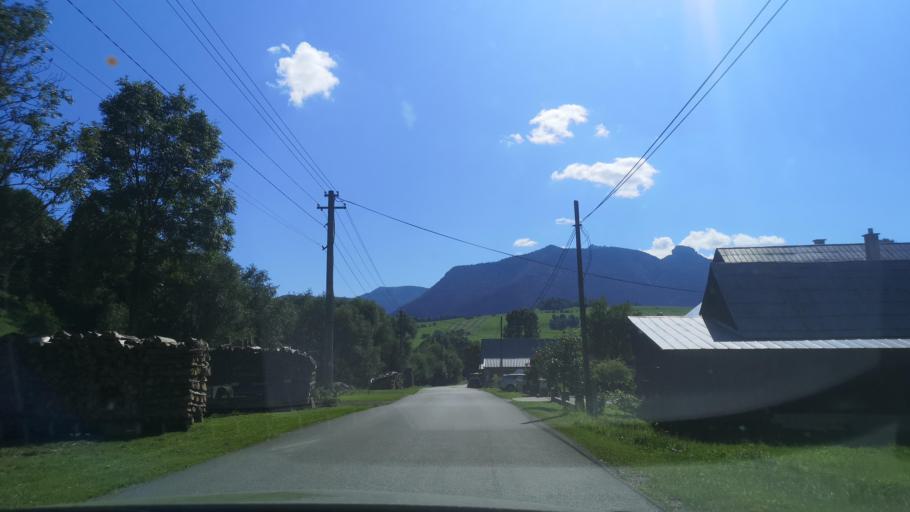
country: SK
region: Zilinsky
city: Oravska Lesna
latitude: 49.2836
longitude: 19.1348
